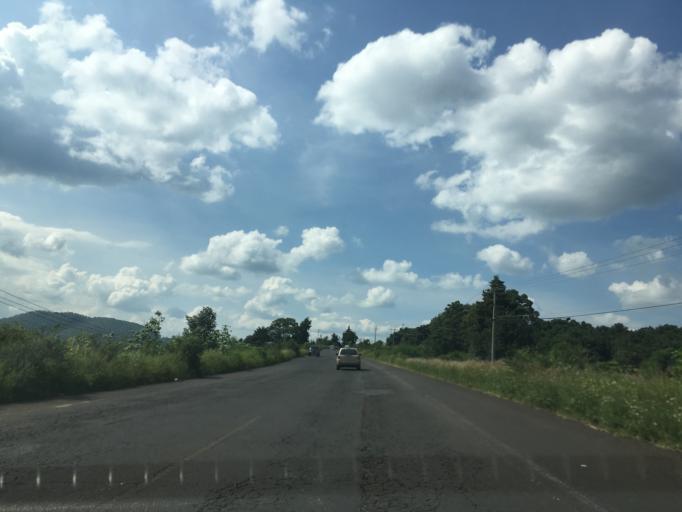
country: MX
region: Michoacan
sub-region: Tingueindin
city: Tingueindin
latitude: 19.7807
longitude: -102.5061
